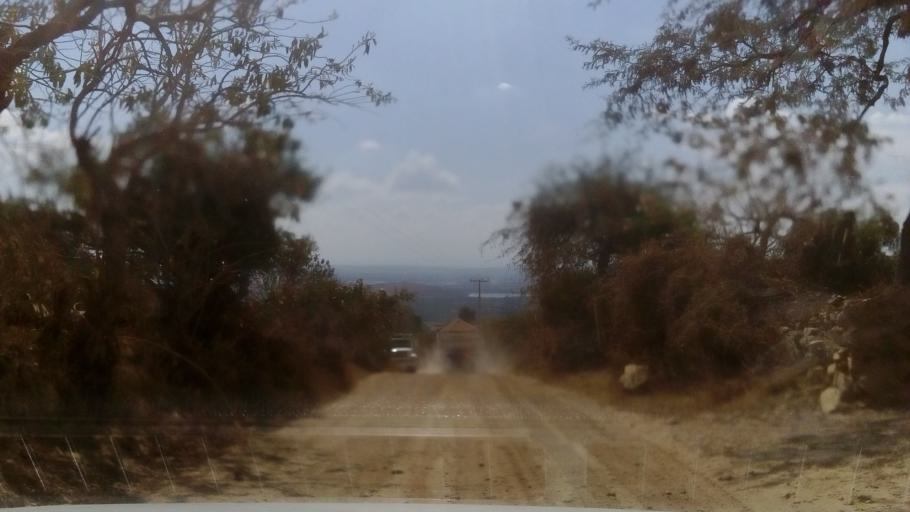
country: MX
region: Guanajuato
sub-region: Silao de la Victoria
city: Loma de Yerbabuena
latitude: 21.0755
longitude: -101.4545
